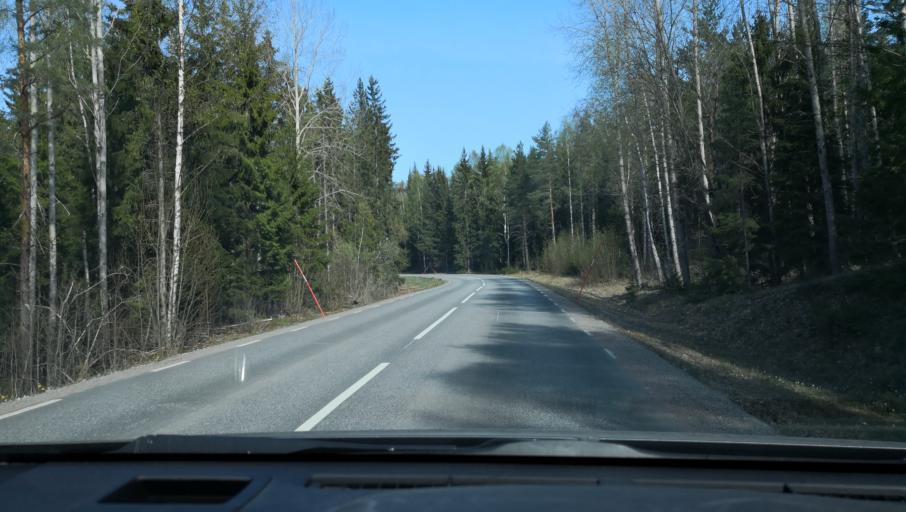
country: SE
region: Vaestmanland
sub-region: Sala Kommun
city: Sala
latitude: 59.9946
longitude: 16.6500
